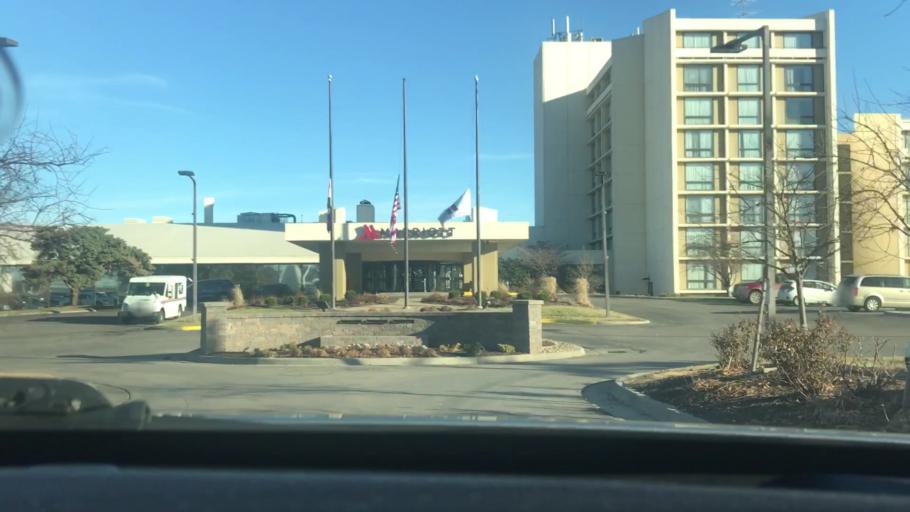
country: US
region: Missouri
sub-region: Platte County
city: Weatherby Lake
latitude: 39.3103
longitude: -94.7147
